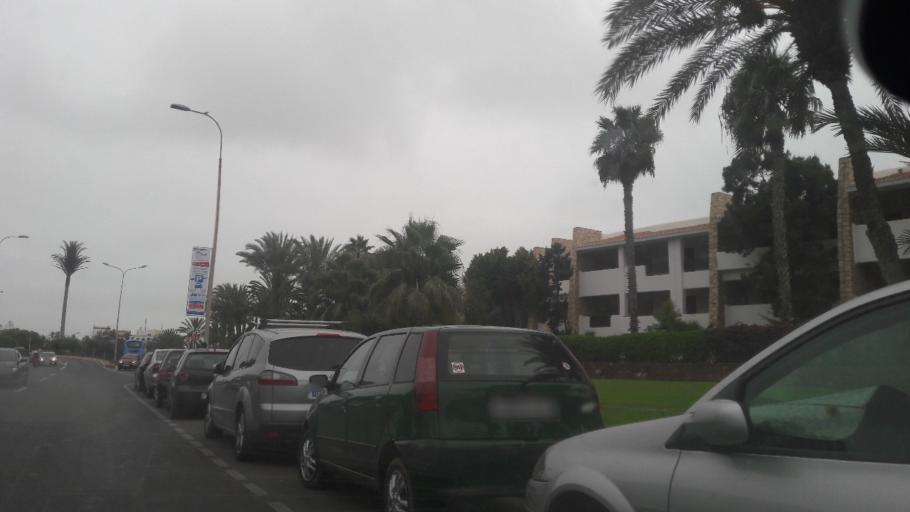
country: MA
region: Souss-Massa-Draa
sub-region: Agadir-Ida-ou-Tnan
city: Agadir
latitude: 30.4001
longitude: -9.5975
